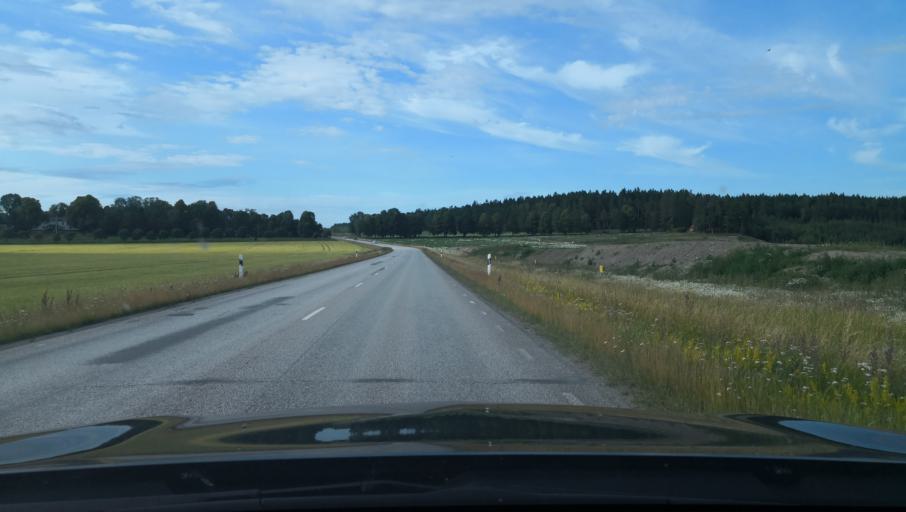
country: SE
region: Uppsala
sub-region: Habo Kommun
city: Balsta
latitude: 59.6120
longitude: 17.5004
